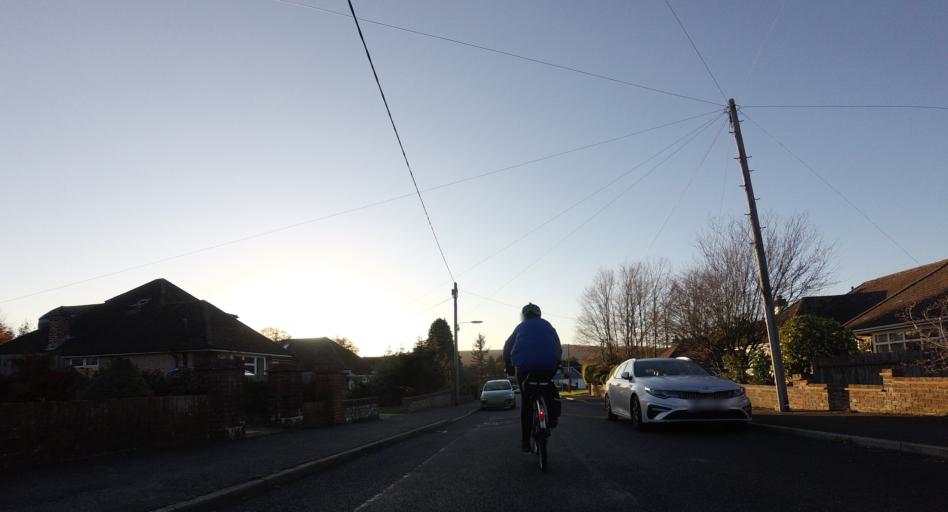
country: GB
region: England
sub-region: West Sussex
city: Steyning
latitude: 50.8857
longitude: -0.3170
